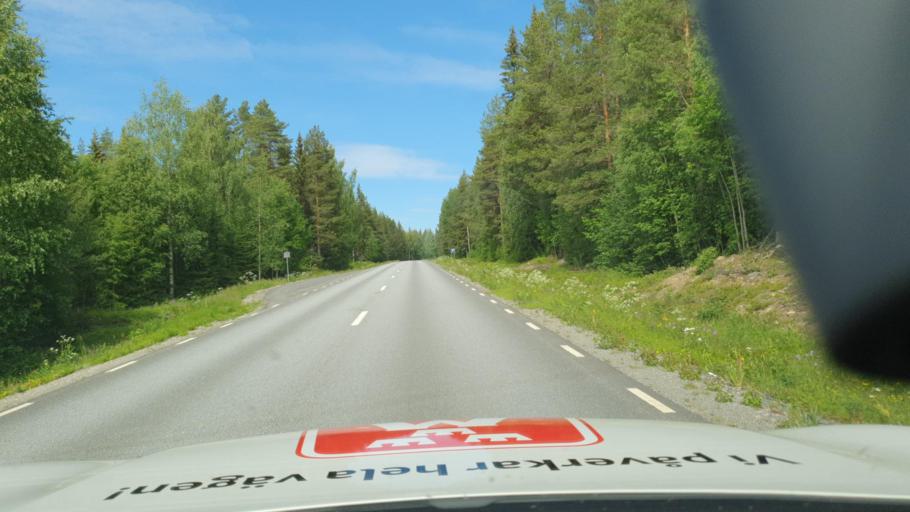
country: SE
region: Vaesterbotten
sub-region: Skelleftea Kommun
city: Forsbacka
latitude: 64.7112
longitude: 20.4263
